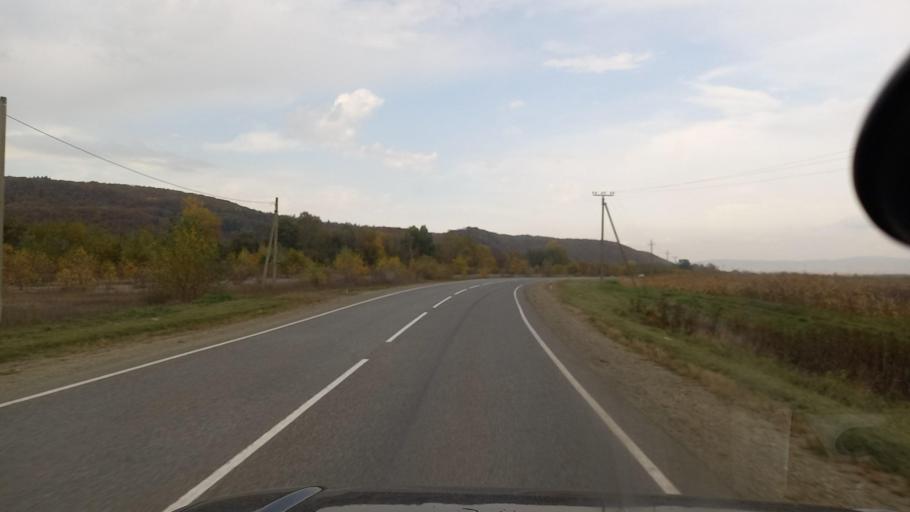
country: RU
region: Krasnodarskiy
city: Shedok
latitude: 44.2284
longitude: 40.8561
